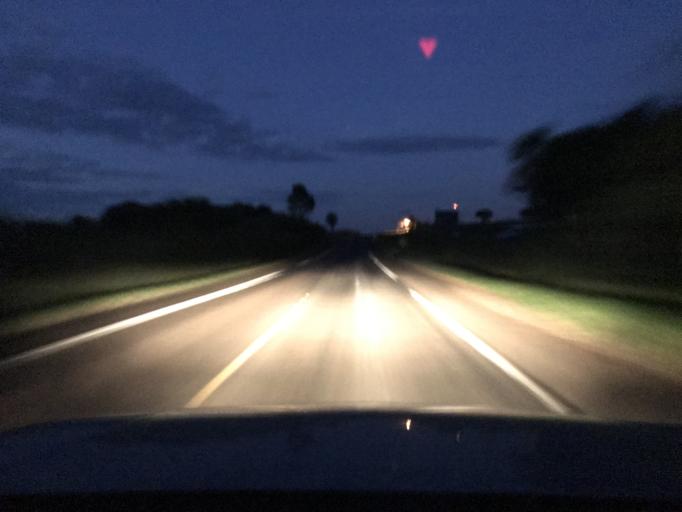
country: PY
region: Canindeyu
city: Salto del Guaira
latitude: -24.1038
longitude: -54.2334
